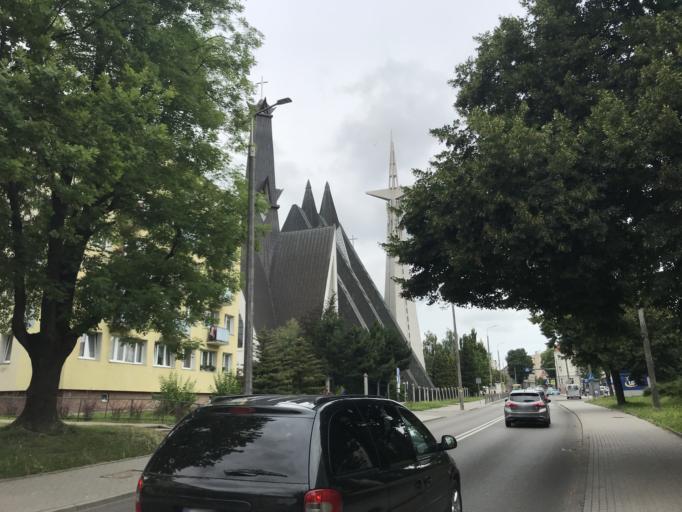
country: PL
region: Warmian-Masurian Voivodeship
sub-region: Powiat elblaski
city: Elblag
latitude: 54.1692
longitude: 19.4012
